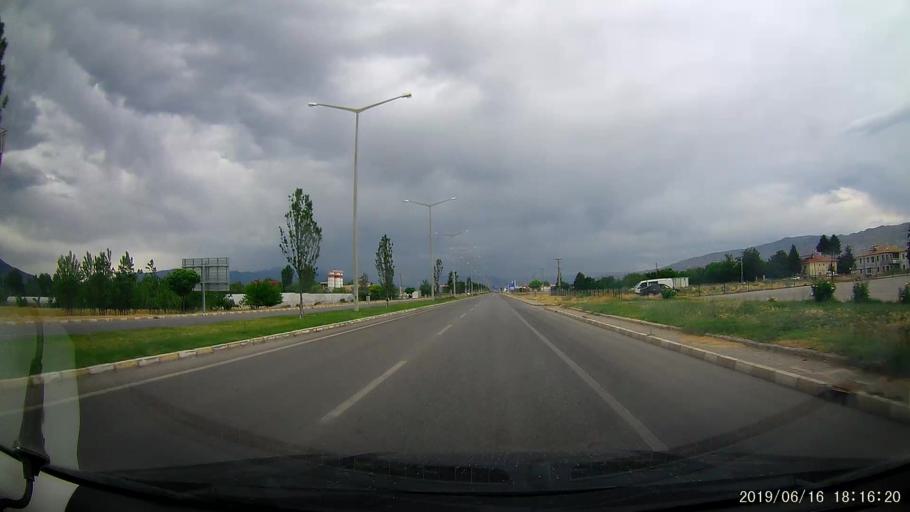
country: TR
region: Erzincan
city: Erzincan
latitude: 39.7278
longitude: 39.5493
